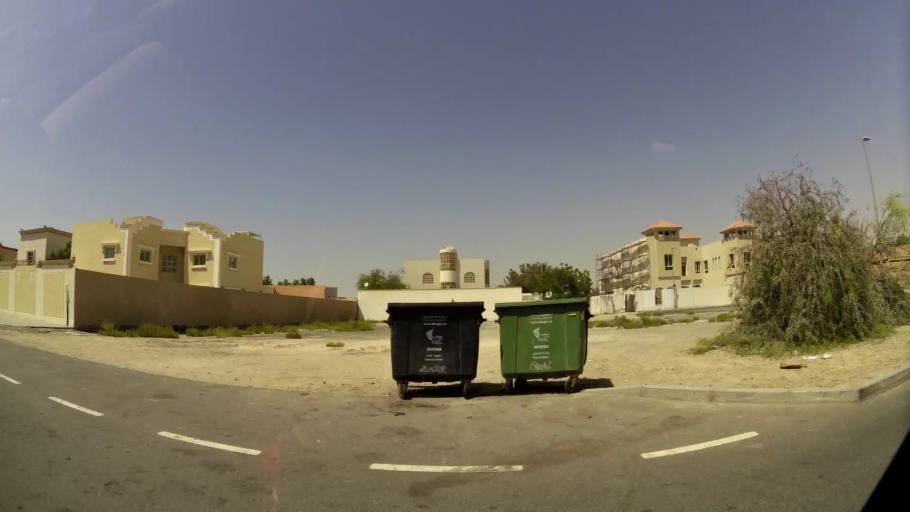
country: AE
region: Dubai
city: Dubai
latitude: 25.1024
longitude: 55.2119
